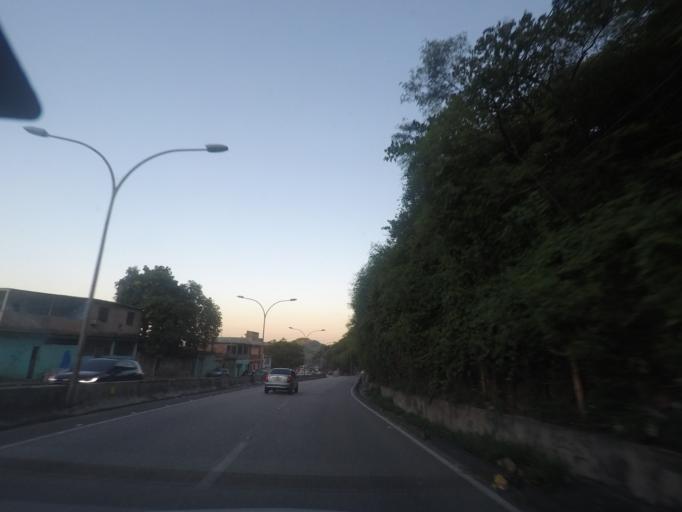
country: BR
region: Rio de Janeiro
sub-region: Rio De Janeiro
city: Rio de Janeiro
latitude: -22.9171
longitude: -43.2780
